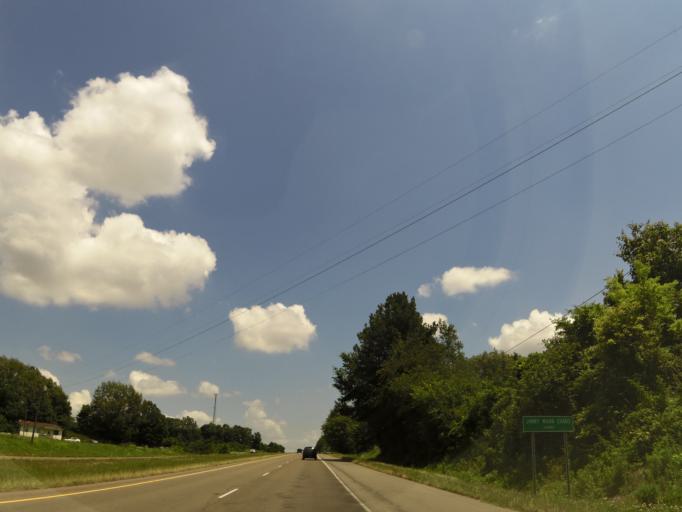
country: US
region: Tennessee
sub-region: Lauderdale County
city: Halls
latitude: 35.9131
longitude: -89.2669
